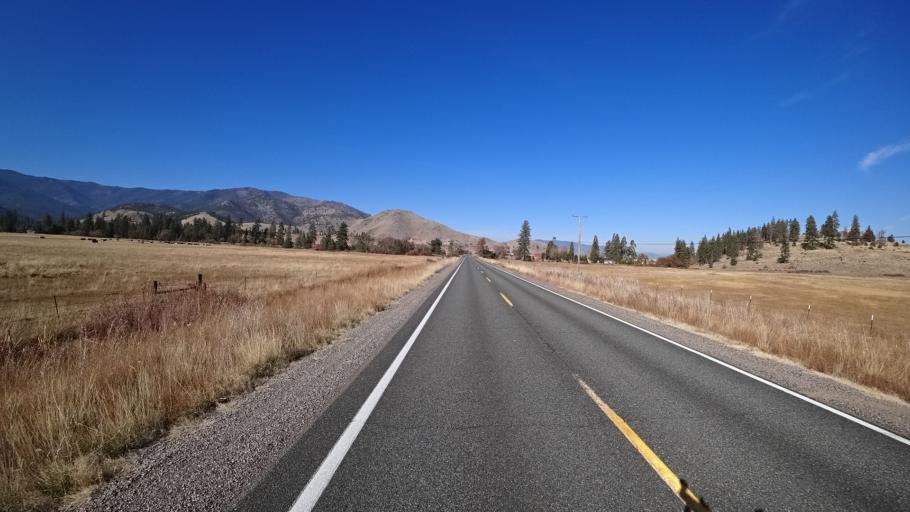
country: US
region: California
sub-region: Siskiyou County
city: Weed
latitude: 41.4465
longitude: -122.4467
